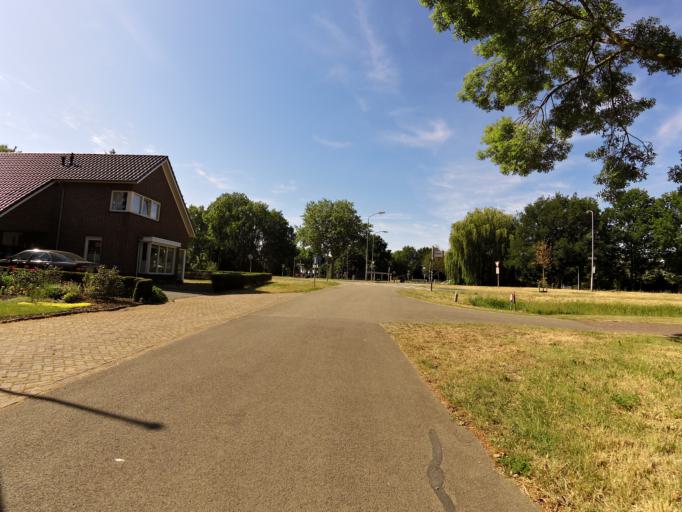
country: NL
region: Gelderland
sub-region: Gemeente Duiven
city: Duiven
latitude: 51.9462
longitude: 6.0377
